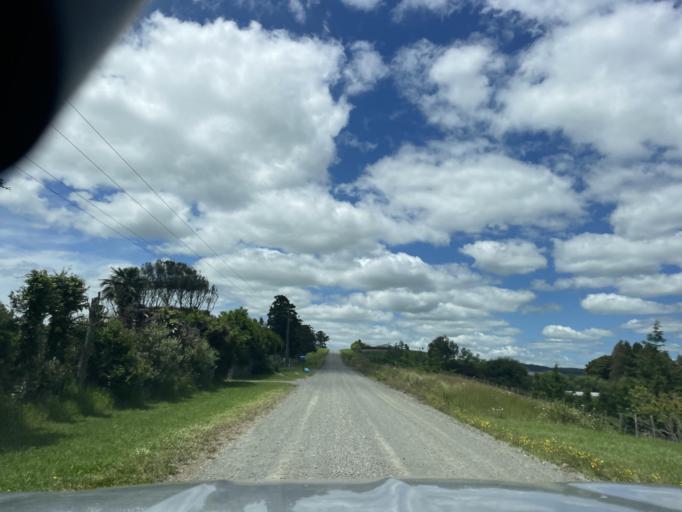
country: NZ
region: Auckland
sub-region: Auckland
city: Wellsford
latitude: -36.1528
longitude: 174.5201
